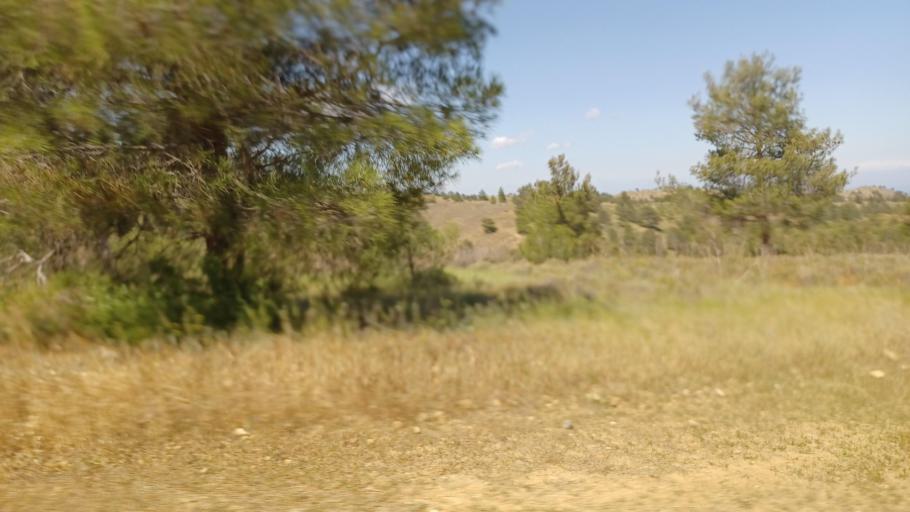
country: CY
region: Lefkosia
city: Astromeritis
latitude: 35.0580
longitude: 33.0235
